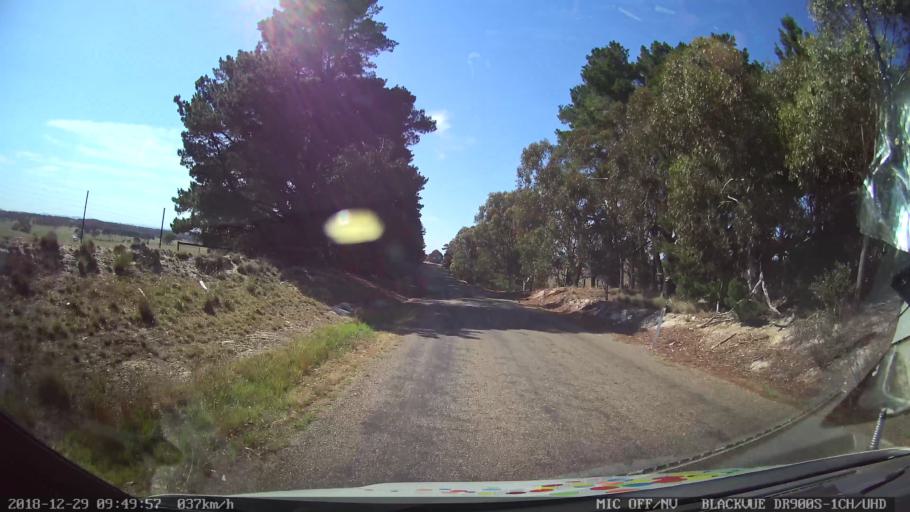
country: AU
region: New South Wales
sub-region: Upper Lachlan Shire
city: Crookwell
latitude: -34.7179
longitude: 149.4565
